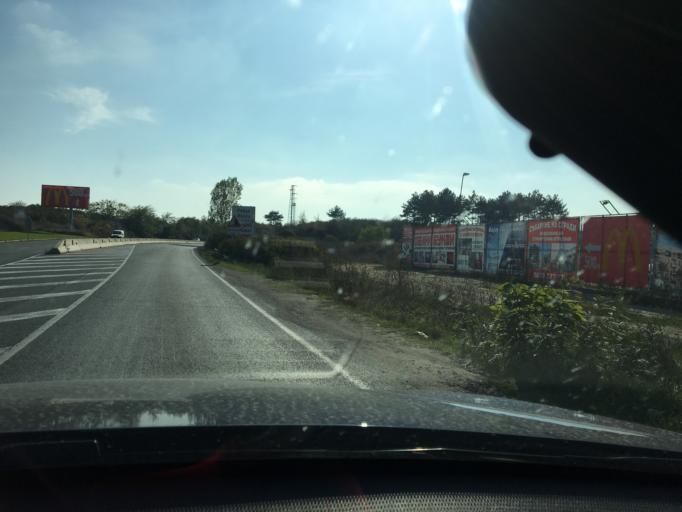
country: BG
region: Burgas
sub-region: Obshtina Nesebur
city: Ravda
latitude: 42.6626
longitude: 27.6925
